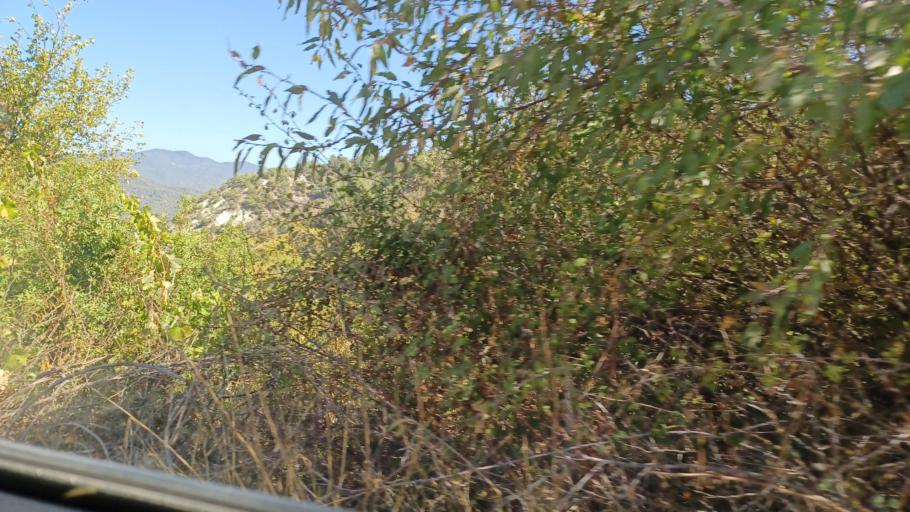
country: CY
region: Pafos
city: Mesogi
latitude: 34.9081
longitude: 32.6259
